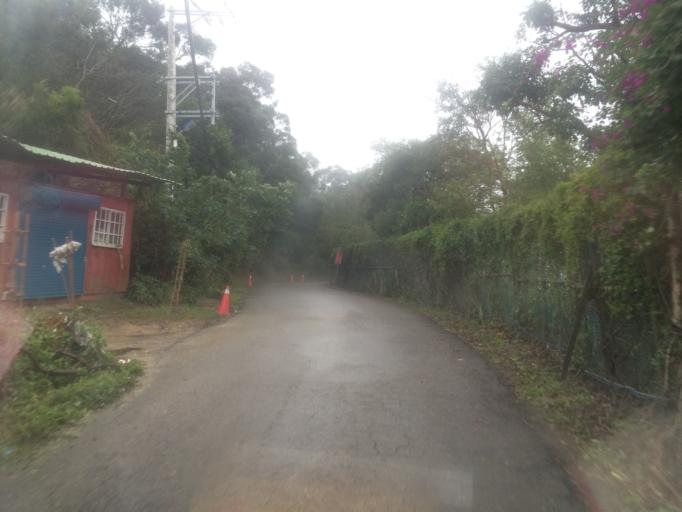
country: TW
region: Taiwan
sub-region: Hsinchu
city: Hsinchu
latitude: 24.7661
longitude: 120.9648
